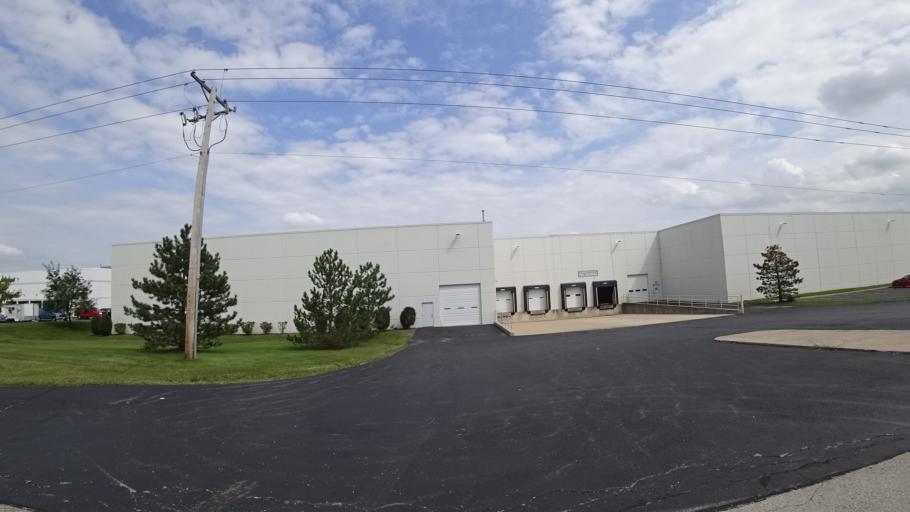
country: US
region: Illinois
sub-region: Cook County
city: Tinley Park
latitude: 41.5541
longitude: -87.8023
